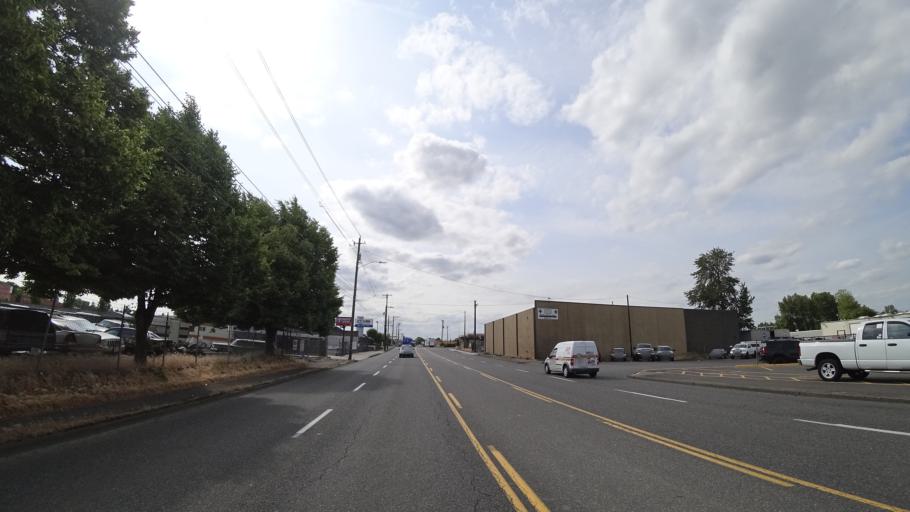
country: US
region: Oregon
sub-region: Multnomah County
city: Portland
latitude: 45.5793
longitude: -122.6552
